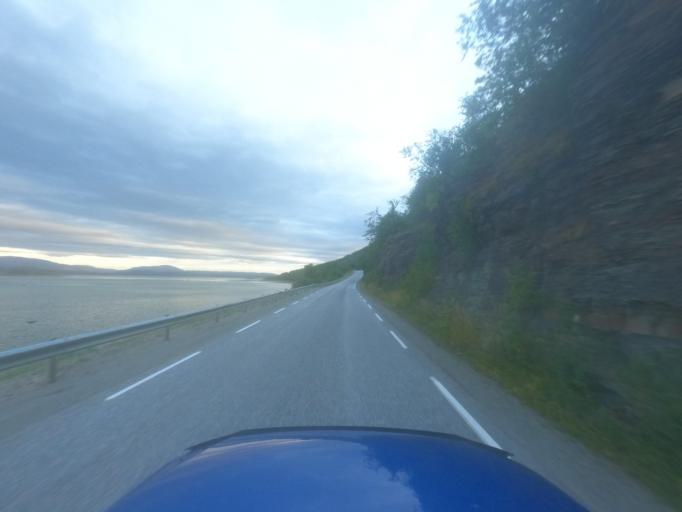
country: NO
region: Finnmark Fylke
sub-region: Porsanger
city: Lakselv
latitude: 70.1280
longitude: 24.9166
